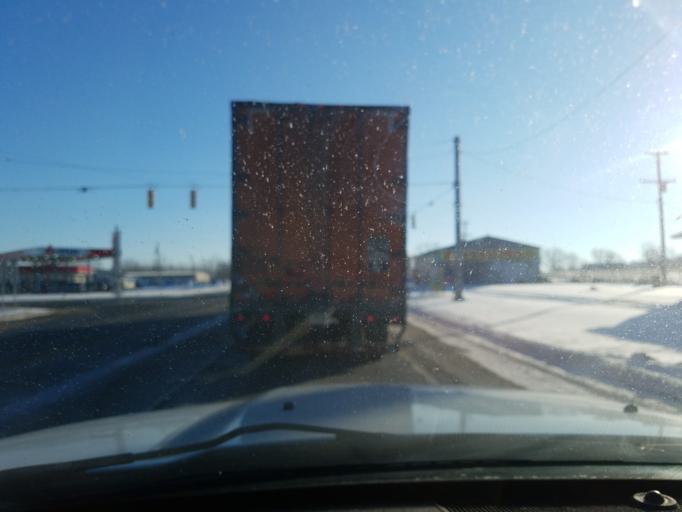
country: US
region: Indiana
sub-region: Noble County
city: Rome City
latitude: 41.4528
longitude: -85.3713
